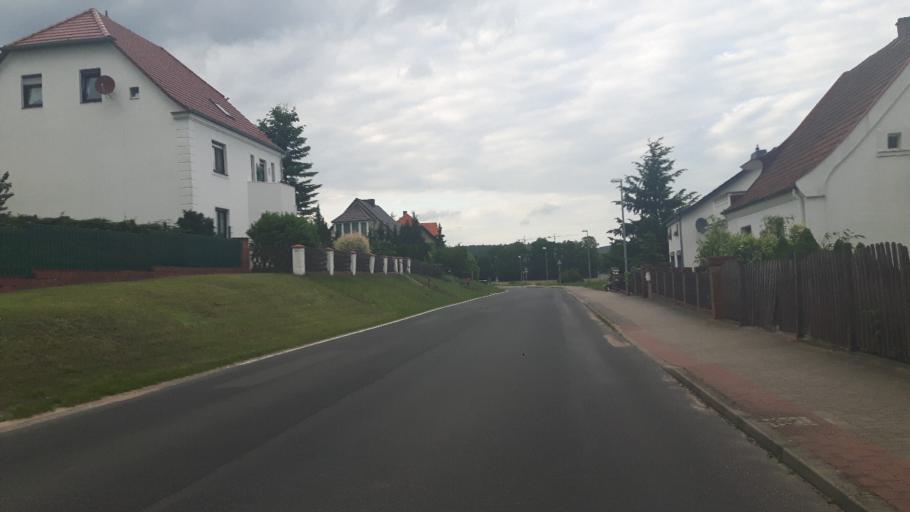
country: DE
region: Brandenburg
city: Niederfinow
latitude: 52.8374
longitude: 13.9367
